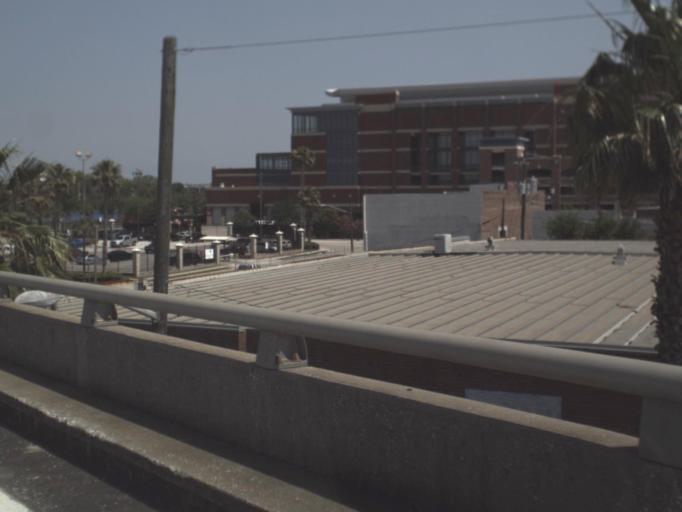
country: US
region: Florida
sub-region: Duval County
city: Jacksonville
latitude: 30.3232
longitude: -81.6450
